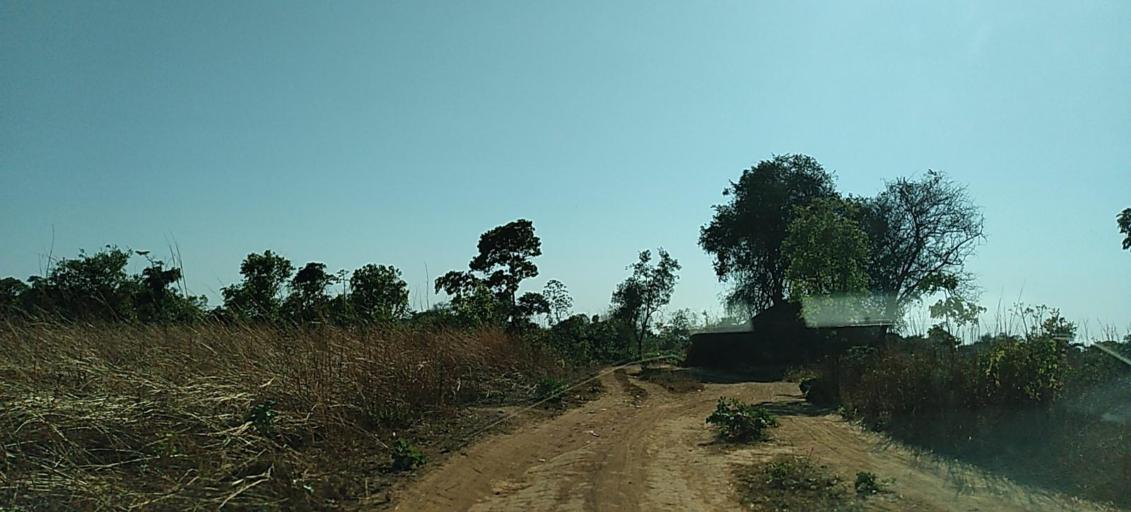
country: ZM
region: Copperbelt
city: Chililabombwe
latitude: -12.3692
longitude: 27.9069
